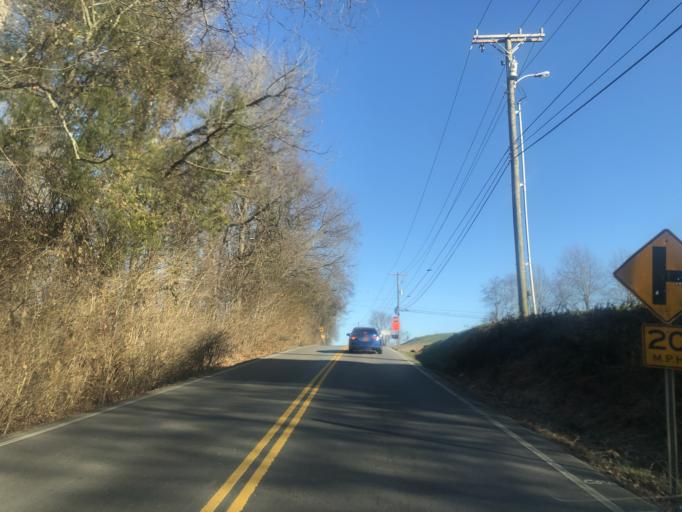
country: US
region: Tennessee
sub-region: Williamson County
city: Nolensville
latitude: 36.0309
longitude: -86.6620
